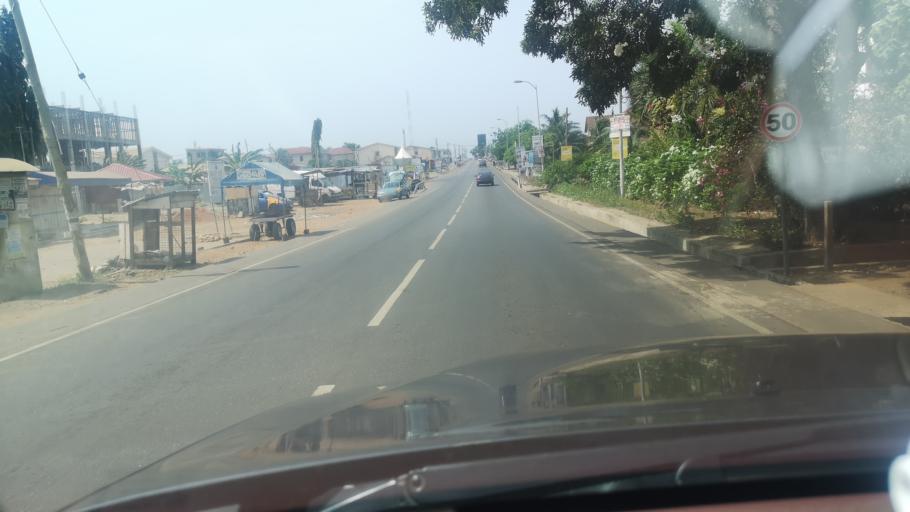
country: GH
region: Greater Accra
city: Nungua
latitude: 5.6439
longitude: -0.0763
